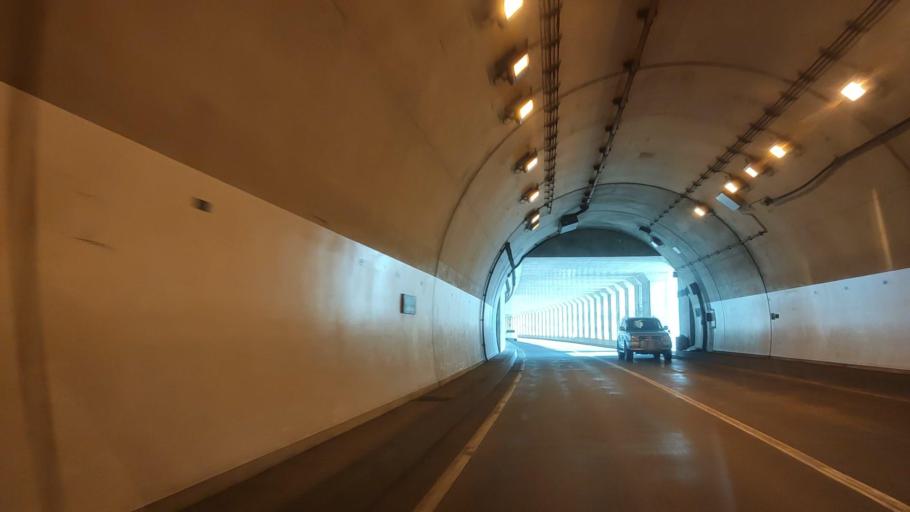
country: JP
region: Hokkaido
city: Rumoi
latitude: 43.6736
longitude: 141.3470
